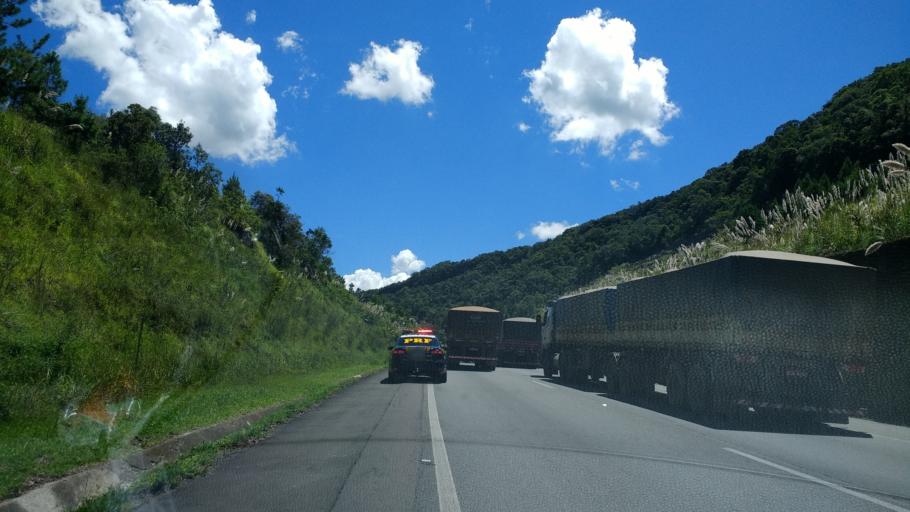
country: BR
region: Parana
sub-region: Campo Largo
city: Campo Largo
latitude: -25.4566
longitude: -49.6364
